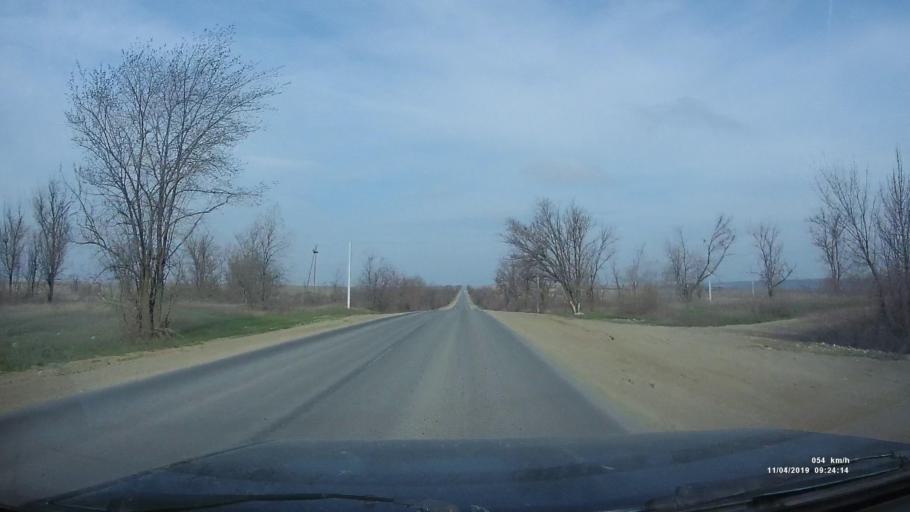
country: RU
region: Rostov
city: Staraya Stanitsa
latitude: 48.2482
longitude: 40.3843
